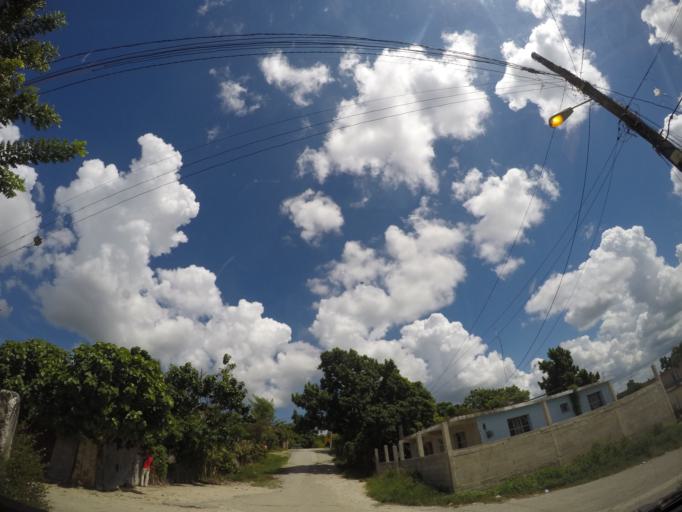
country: CU
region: La Habana
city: Cerro
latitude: 23.1195
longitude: -82.3761
